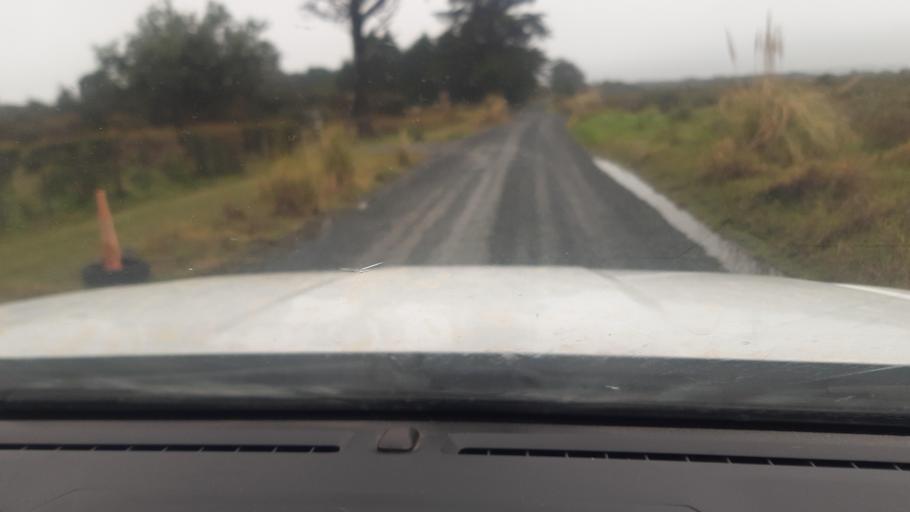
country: NZ
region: Northland
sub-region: Far North District
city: Kaitaia
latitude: -34.9122
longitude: 173.2686
